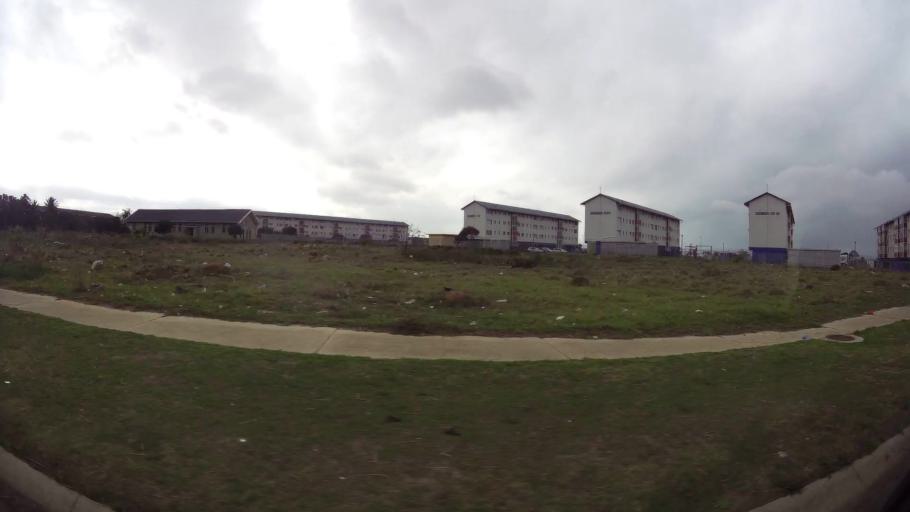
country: ZA
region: Eastern Cape
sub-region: Nelson Mandela Bay Metropolitan Municipality
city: Port Elizabeth
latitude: -33.9029
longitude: 25.5551
